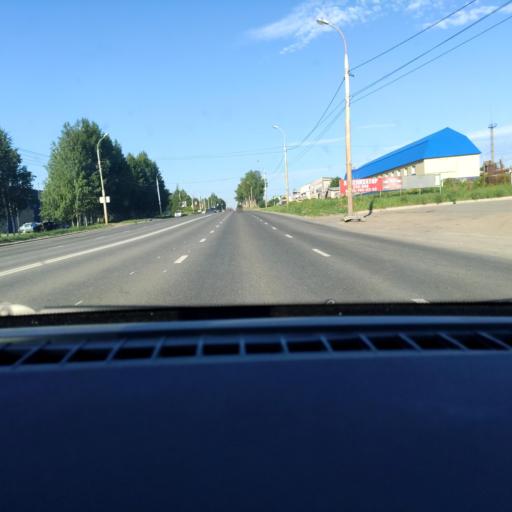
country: RU
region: Udmurtiya
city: Khokhryaki
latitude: 56.9036
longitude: 53.3331
